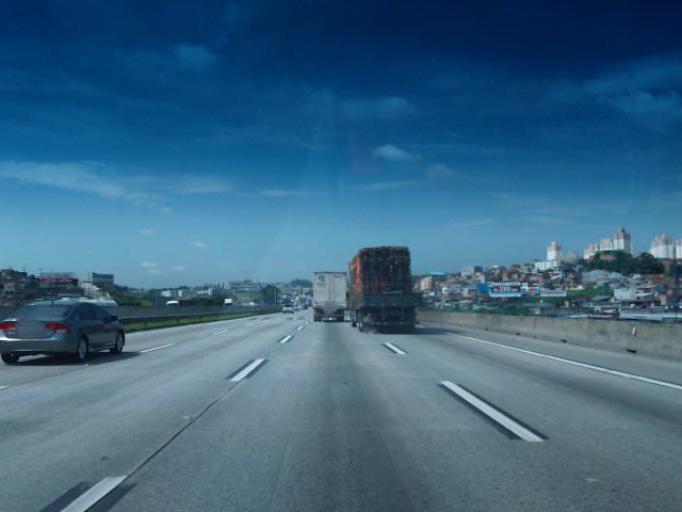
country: BR
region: Sao Paulo
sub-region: Carapicuiba
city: Carapicuiba
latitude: -23.5460
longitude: -46.8200
